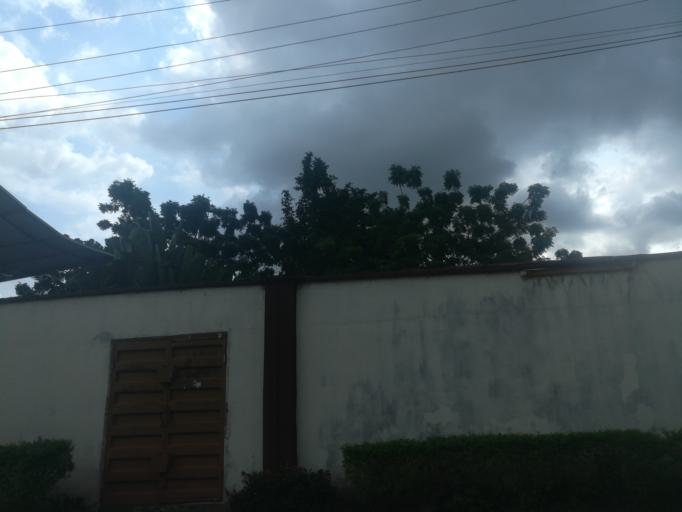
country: NG
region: Lagos
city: Ojota
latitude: 6.5614
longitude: 3.3842
